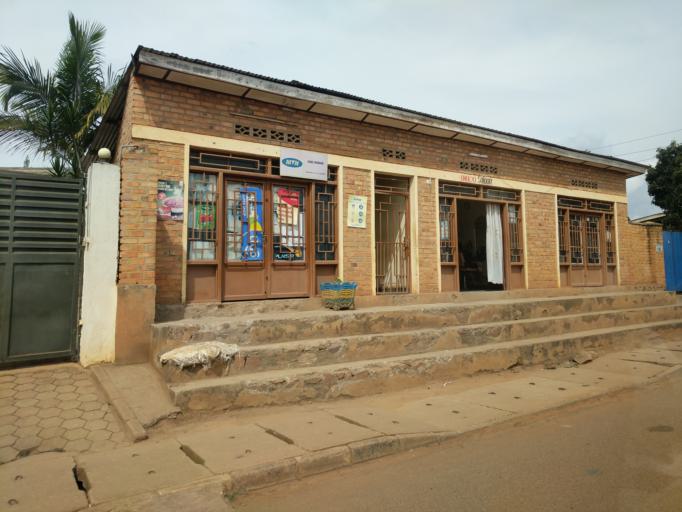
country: RW
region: Kigali
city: Kigali
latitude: -1.9721
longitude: 30.1332
